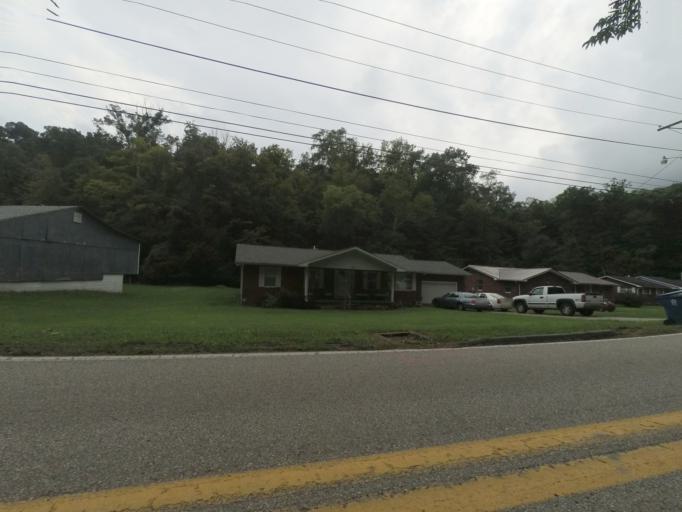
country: US
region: West Virginia
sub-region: Cabell County
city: Huntington
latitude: 38.3907
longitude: -82.4380
